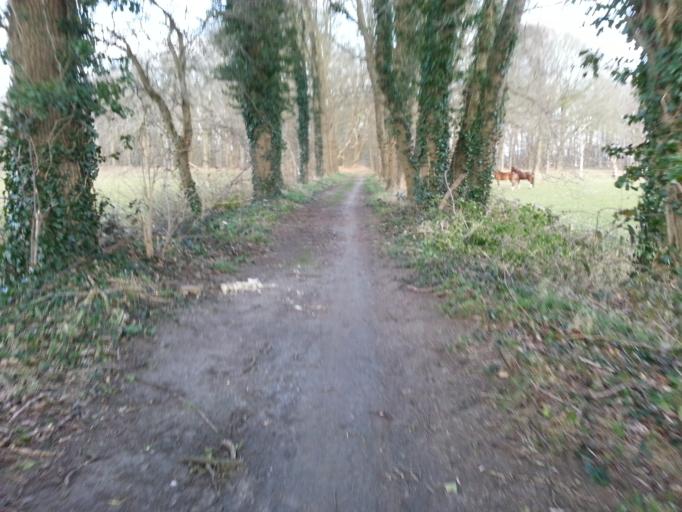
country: NL
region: Utrecht
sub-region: Gemeente Woudenberg
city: Woudenberg
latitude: 52.0925
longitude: 5.4555
